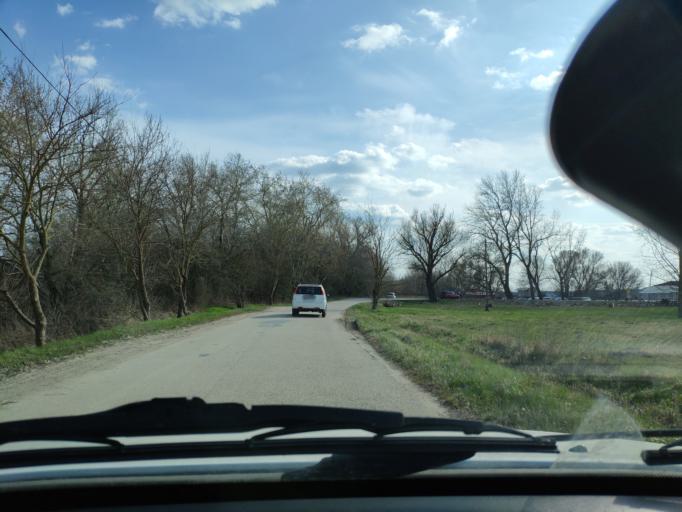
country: HU
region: Fejer
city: Adony
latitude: 47.1143
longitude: 18.8898
